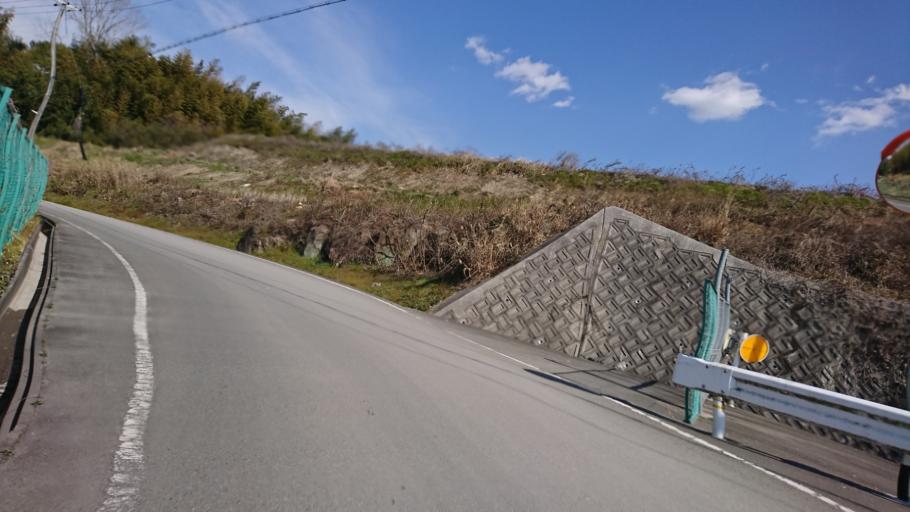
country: JP
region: Hyogo
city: Kakogawacho-honmachi
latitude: 34.8204
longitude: 134.8314
